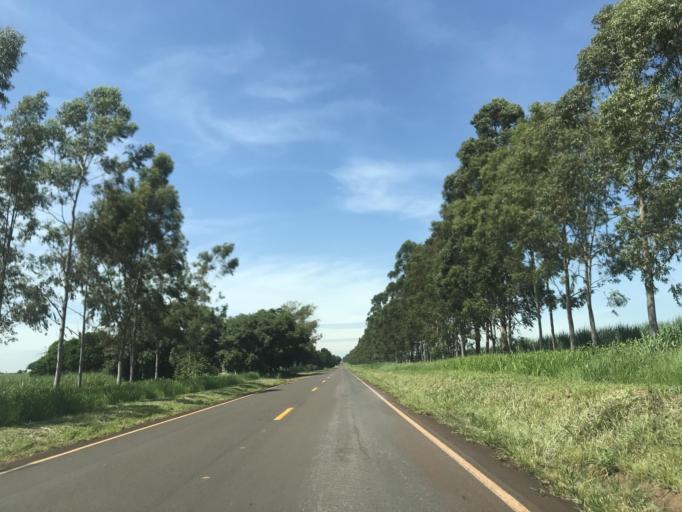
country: BR
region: Parana
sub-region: Paranavai
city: Nova Aurora
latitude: -22.8376
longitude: -52.6565
